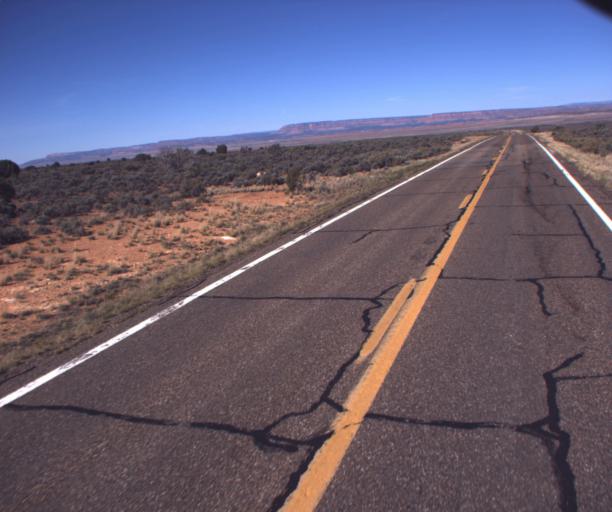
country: US
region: Arizona
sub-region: Coconino County
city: Fredonia
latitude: 36.8844
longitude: -112.3444
